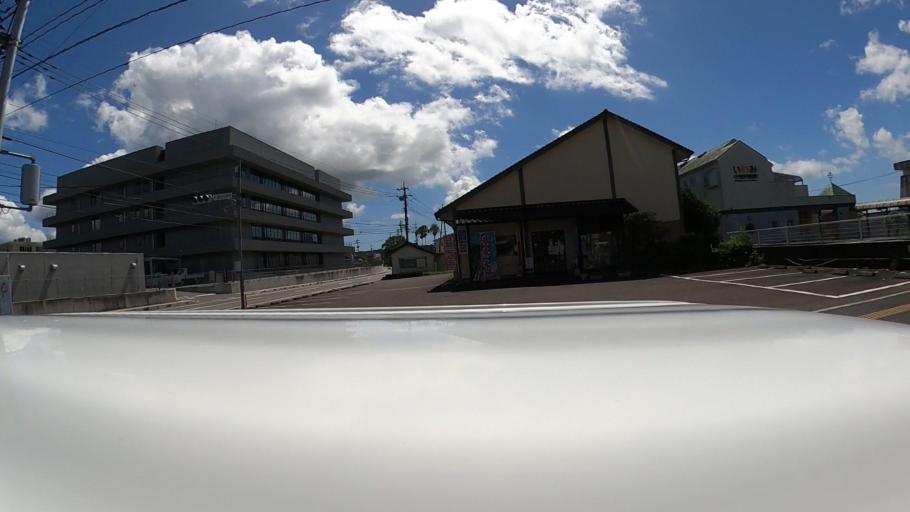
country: JP
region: Miyazaki
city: Tsuma
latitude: 32.1075
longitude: 131.4002
